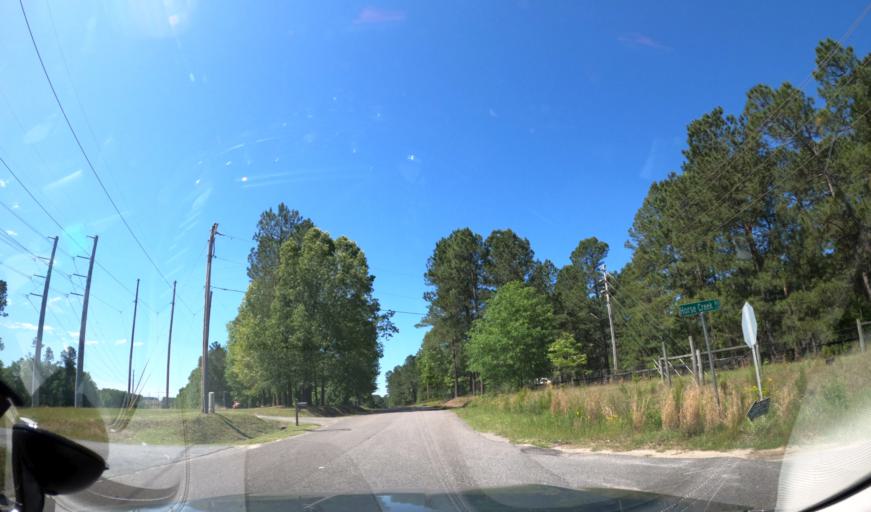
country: US
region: South Carolina
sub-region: Aiken County
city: Langley
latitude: 33.4441
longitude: -81.8090
